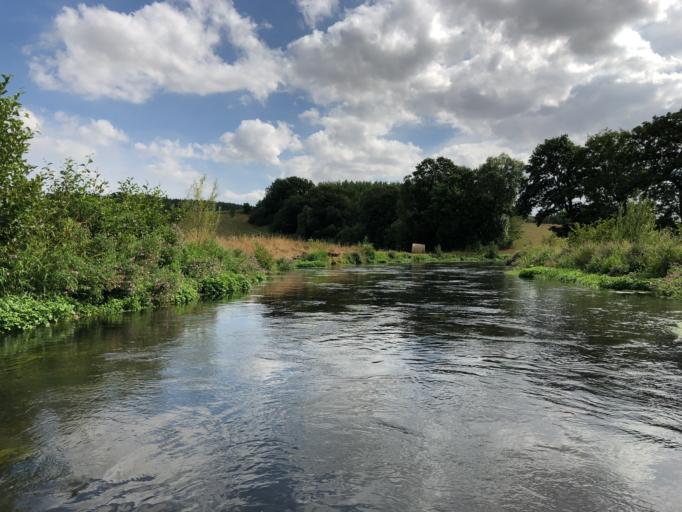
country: DK
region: South Denmark
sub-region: Vejle Kommune
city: Jelling
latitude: 55.6922
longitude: 9.4200
